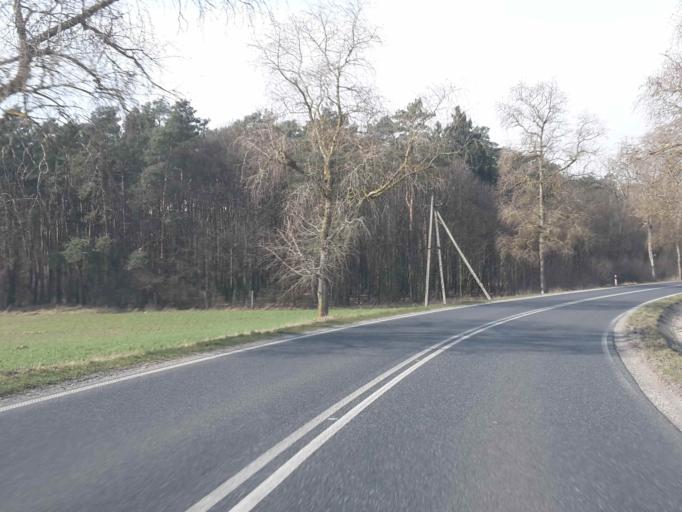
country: PL
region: Kujawsko-Pomorskie
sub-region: Powiat nakielski
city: Naklo nad Notecia
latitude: 53.0994
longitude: 17.6283
